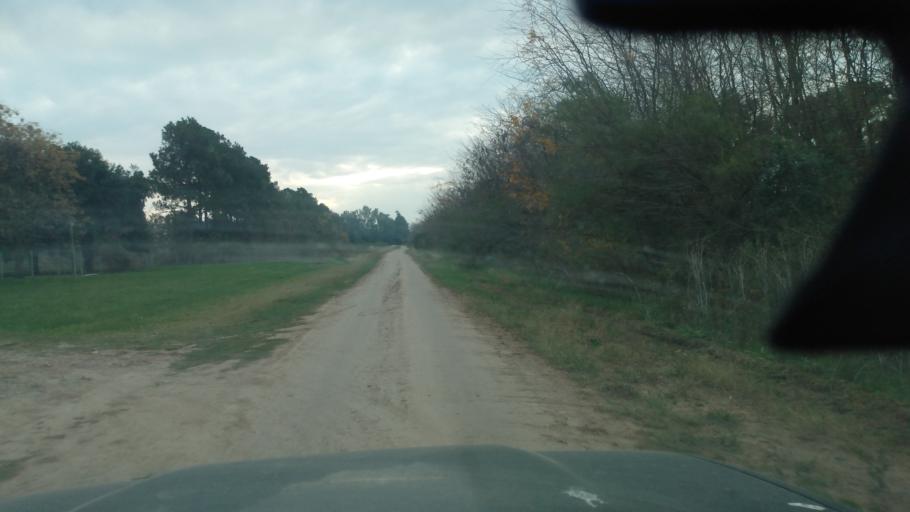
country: AR
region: Buenos Aires
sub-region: Partido de Lujan
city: Lujan
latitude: -34.5626
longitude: -59.1541
